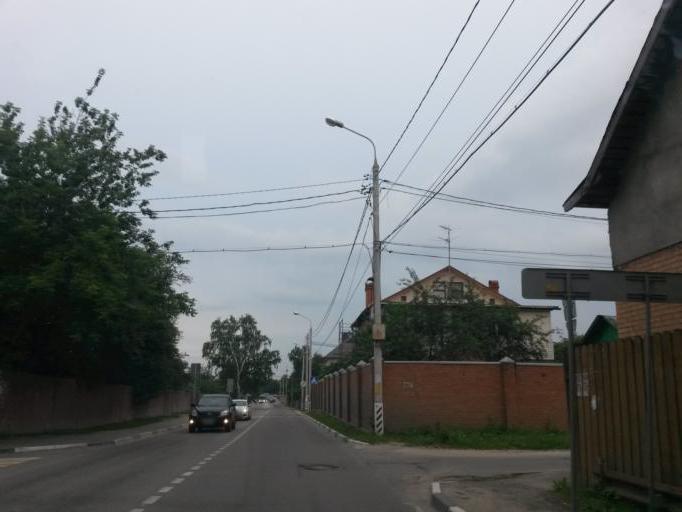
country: RU
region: Moskovskaya
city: Domodedovo
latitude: 55.4517
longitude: 37.7556
